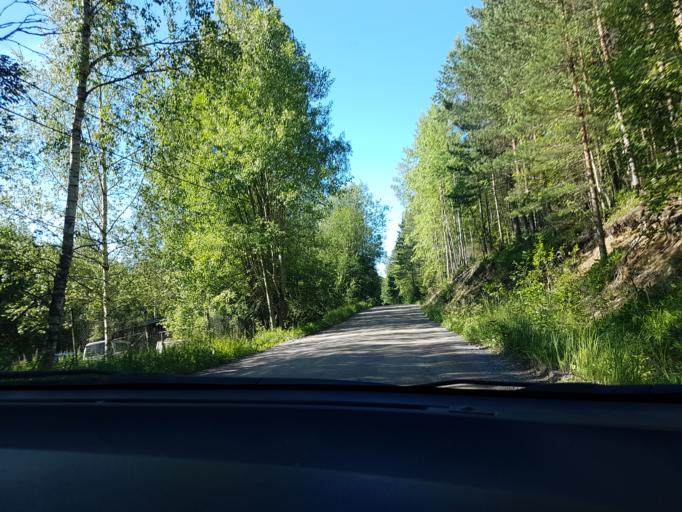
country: FI
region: Uusimaa
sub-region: Helsinki
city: Sibbo
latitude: 60.2757
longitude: 25.2348
